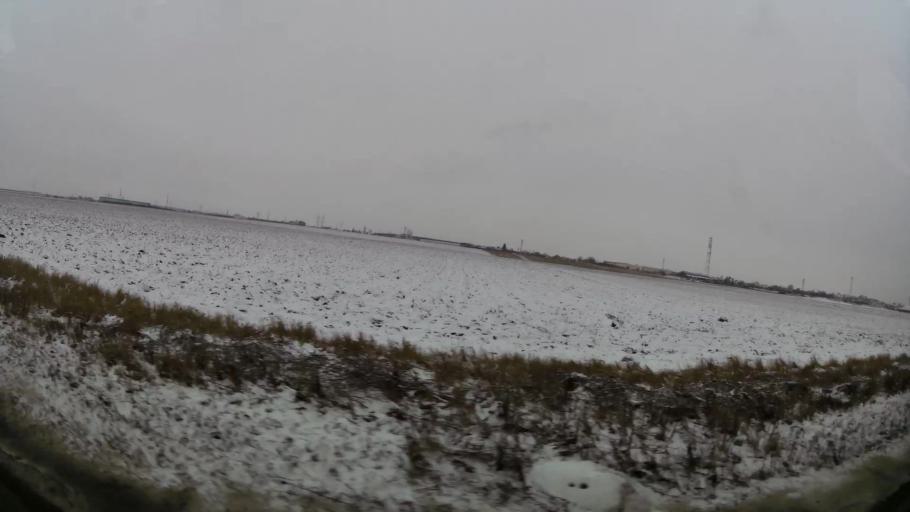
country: RO
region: Dambovita
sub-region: Comuna Ulmi
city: Ulmi
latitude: 44.8920
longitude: 25.5156
